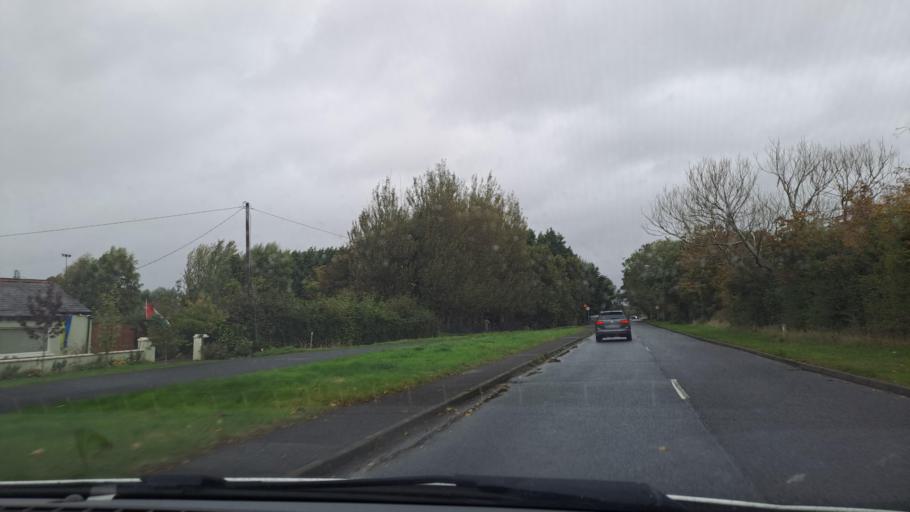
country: IE
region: Leinster
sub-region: Lu
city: Blackrock
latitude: 53.9853
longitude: -6.3708
